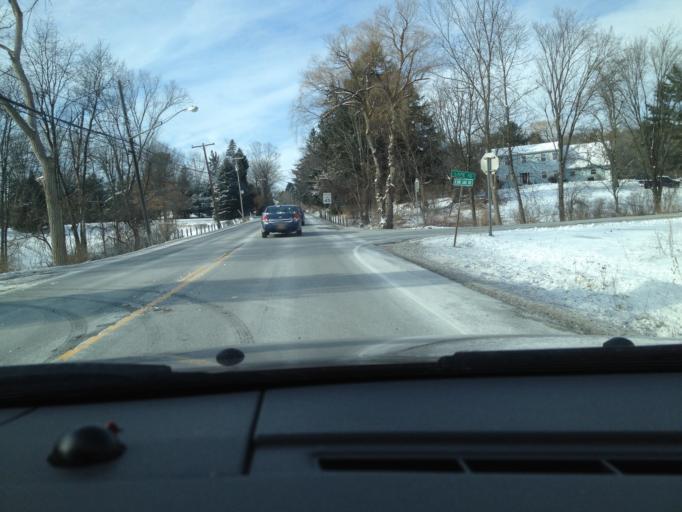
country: US
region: New York
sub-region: Rensselaer County
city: Wynantskill
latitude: 42.6516
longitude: -73.6677
